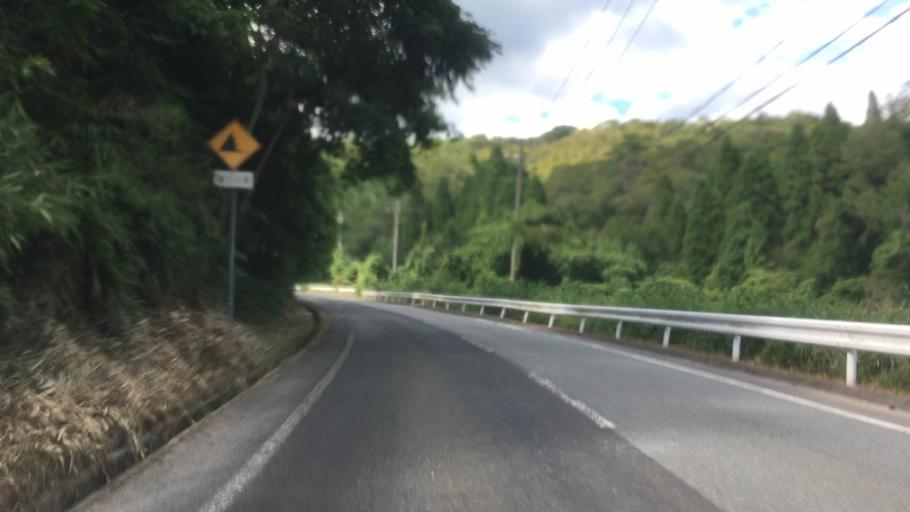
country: JP
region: Hyogo
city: Toyooka
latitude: 35.5126
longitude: 134.7807
